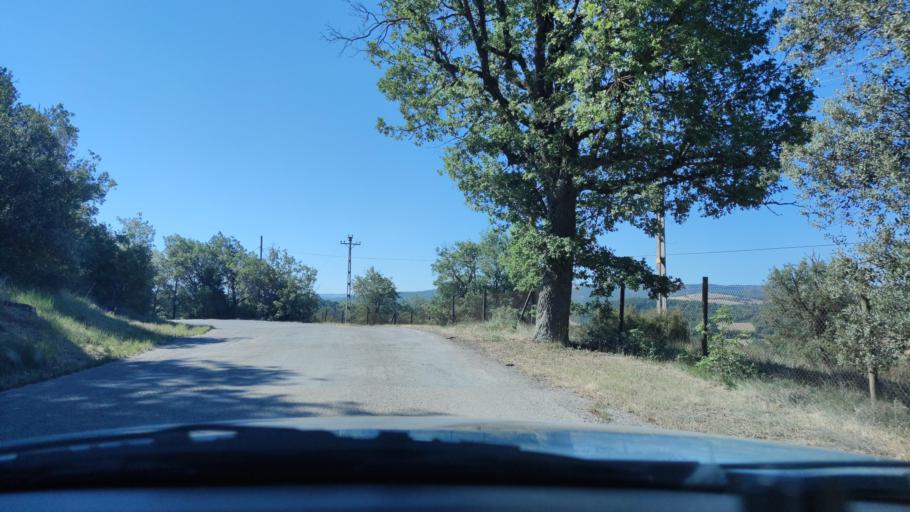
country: ES
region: Catalonia
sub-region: Provincia de Barcelona
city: Cardona
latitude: 41.8887
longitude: 1.5666
